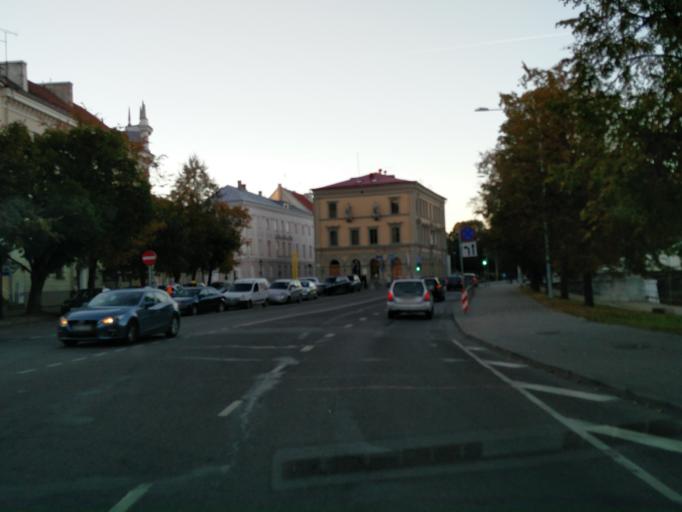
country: EE
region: Tartu
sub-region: Tartu linn
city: Tartu
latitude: 58.3799
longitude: 26.7257
